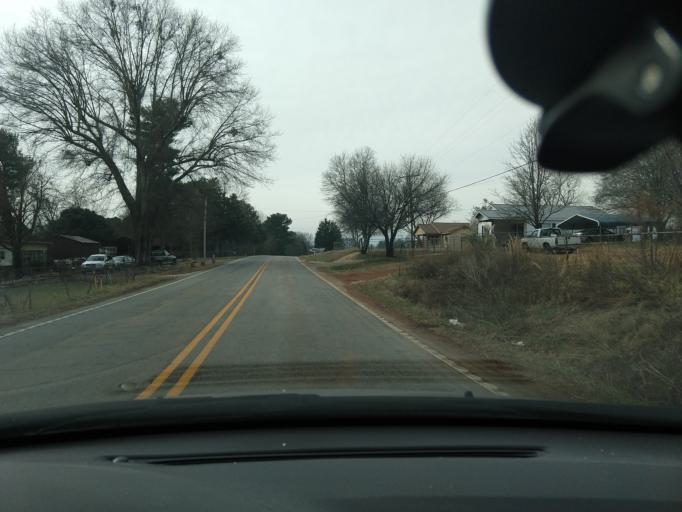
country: US
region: South Carolina
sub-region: Spartanburg County
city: Cowpens
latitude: 35.0331
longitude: -81.8146
